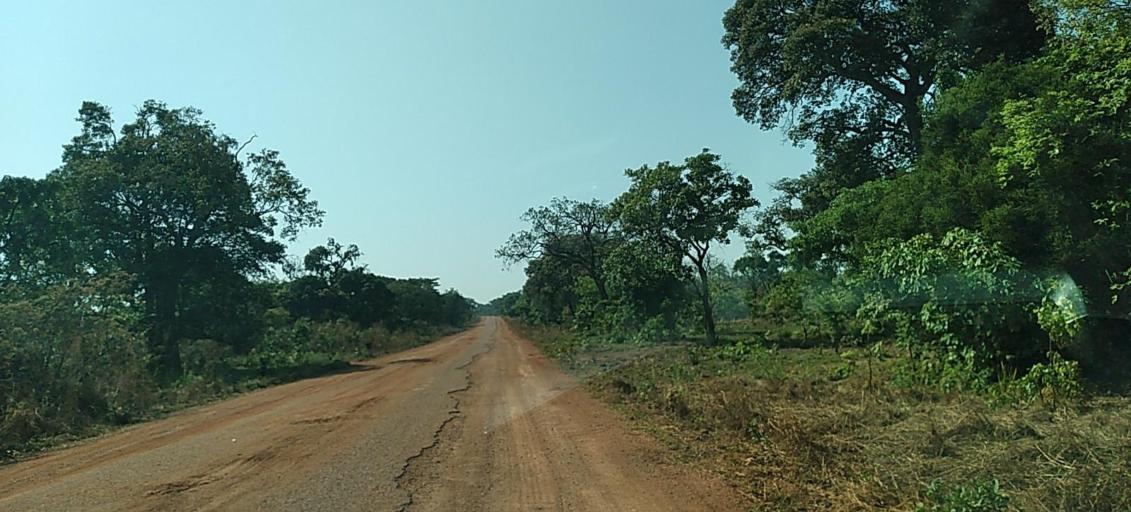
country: ZM
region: North-Western
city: Mwinilunga
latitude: -11.8952
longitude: 25.2714
